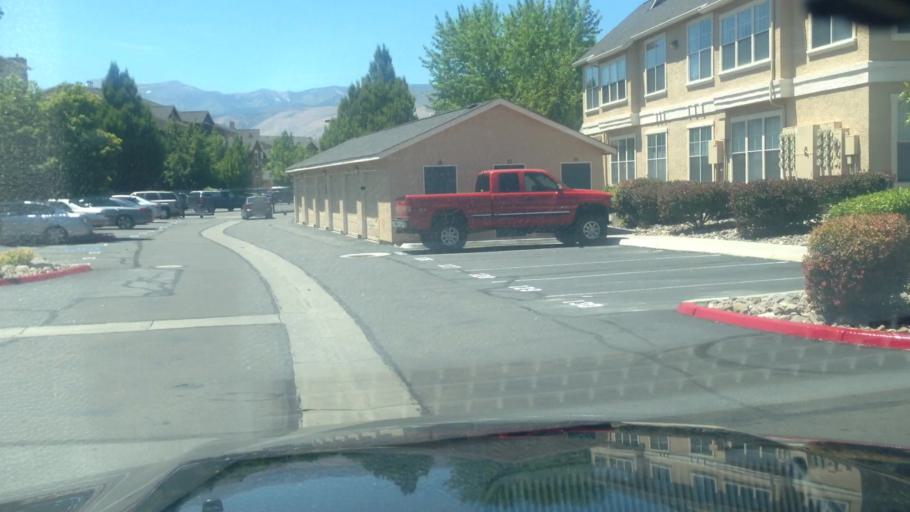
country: US
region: Nevada
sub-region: Washoe County
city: Sparks
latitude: 39.4412
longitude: -119.7523
